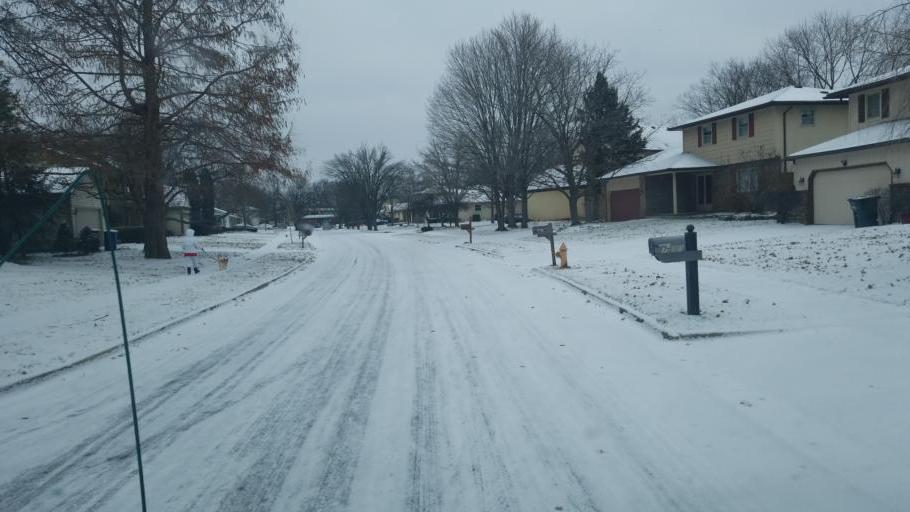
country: US
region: Ohio
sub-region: Franklin County
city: Dublin
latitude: 40.1150
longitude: -83.0764
